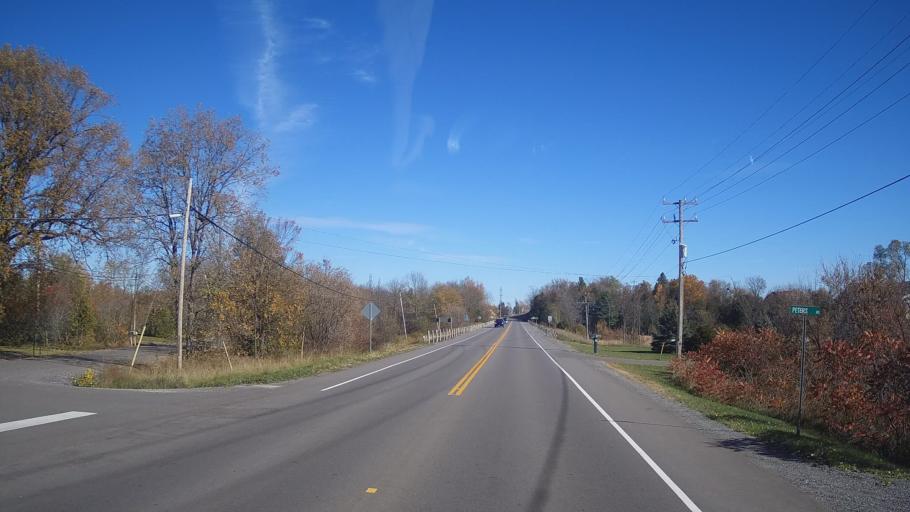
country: CA
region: Ontario
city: Kingston
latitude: 44.4057
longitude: -76.6550
